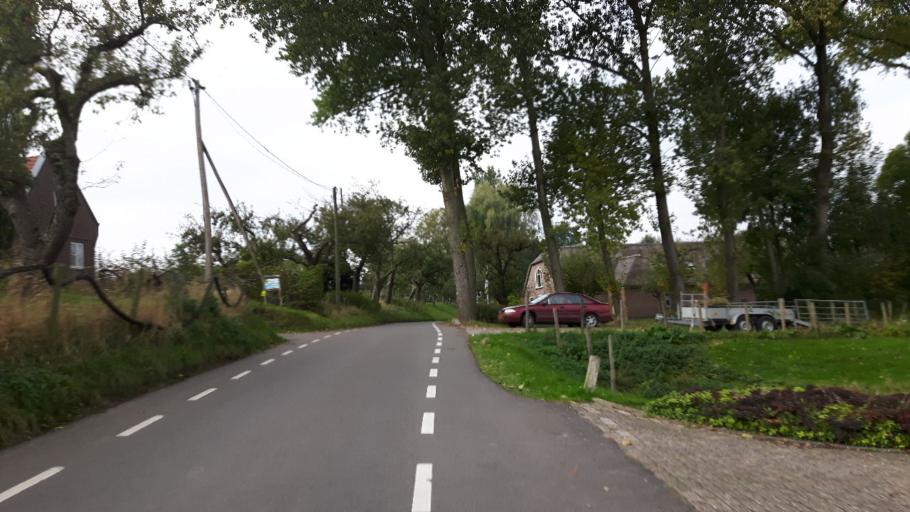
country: NL
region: Utrecht
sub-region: Gemeente Oudewater
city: Oudewater
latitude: 52.0171
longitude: 4.8310
